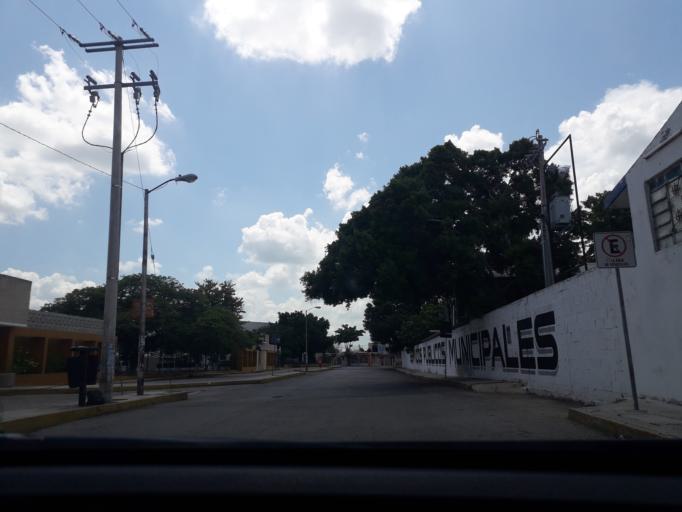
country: MX
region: Yucatan
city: Merida
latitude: 20.9821
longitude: -89.6553
